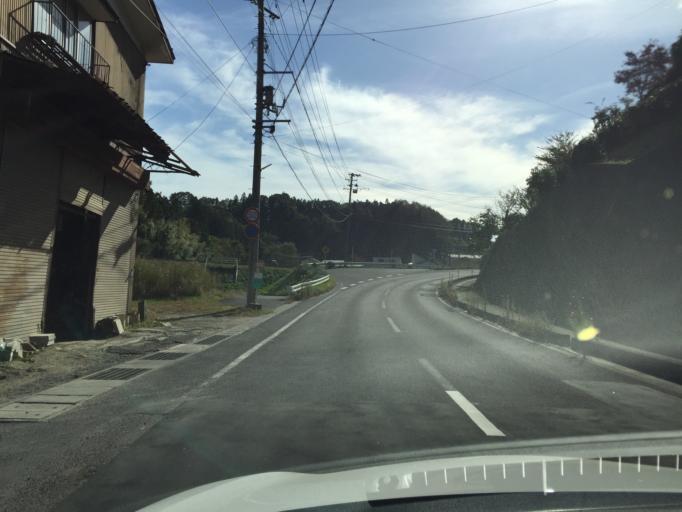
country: JP
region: Fukushima
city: Miharu
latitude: 37.4494
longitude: 140.4870
